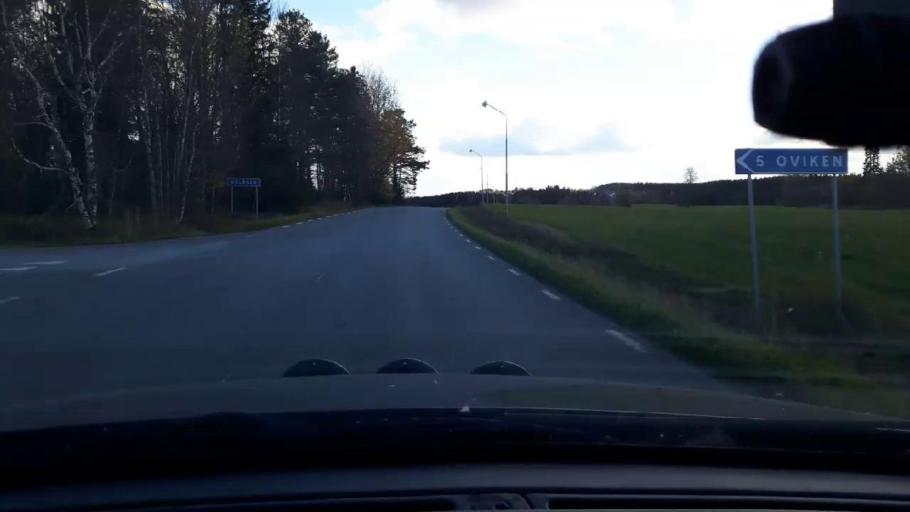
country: SE
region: Jaemtland
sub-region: Bergs Kommun
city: Hoverberg
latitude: 63.0360
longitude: 14.3453
